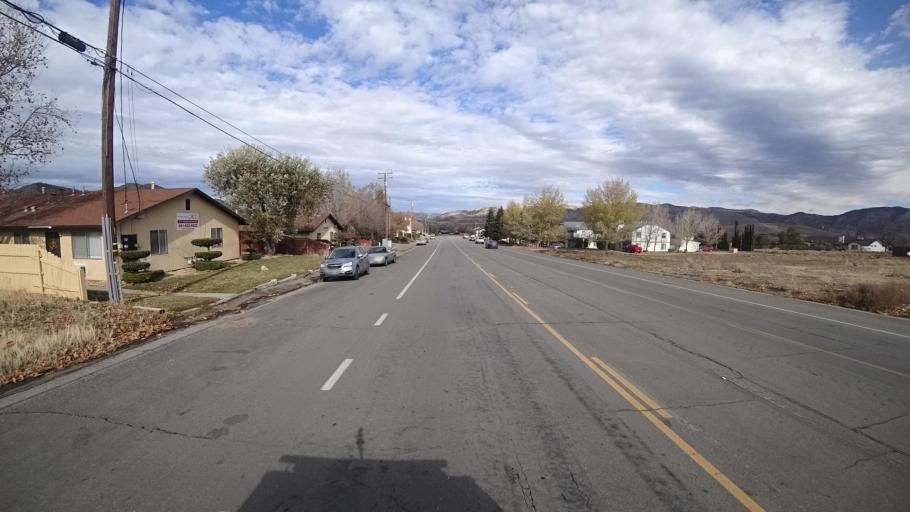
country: US
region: California
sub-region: Kern County
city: Golden Hills
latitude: 35.1258
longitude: -118.4860
